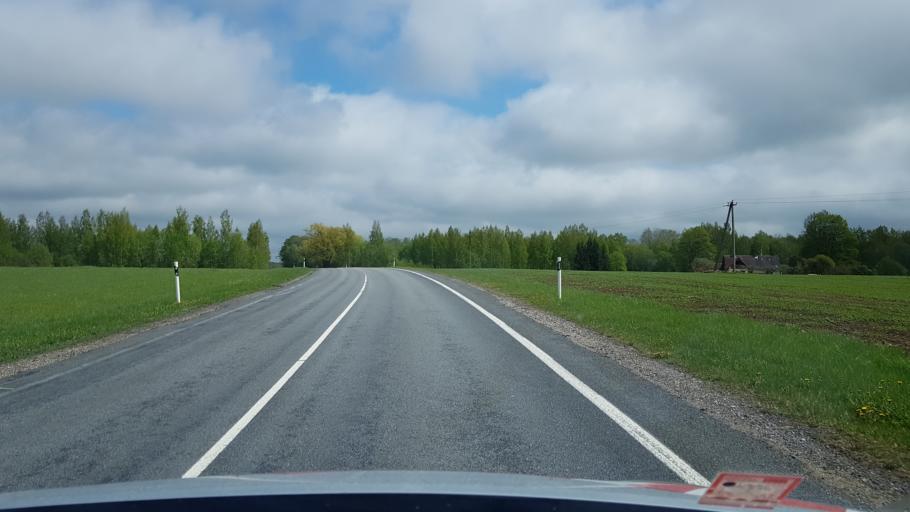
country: EE
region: Viljandimaa
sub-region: Suure-Jaani vald
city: Suure-Jaani
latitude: 58.3513
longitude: 25.3787
